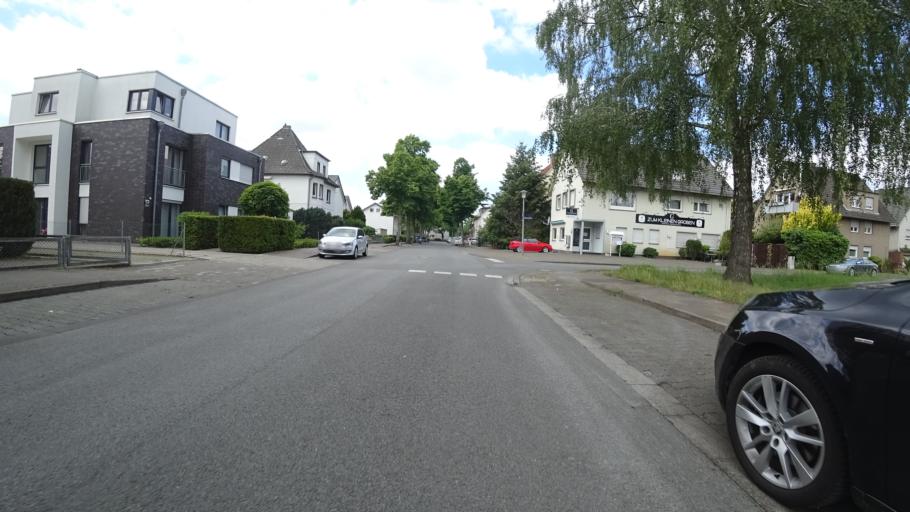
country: DE
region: North Rhine-Westphalia
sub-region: Regierungsbezirk Detmold
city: Guetersloh
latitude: 51.9159
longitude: 8.3762
